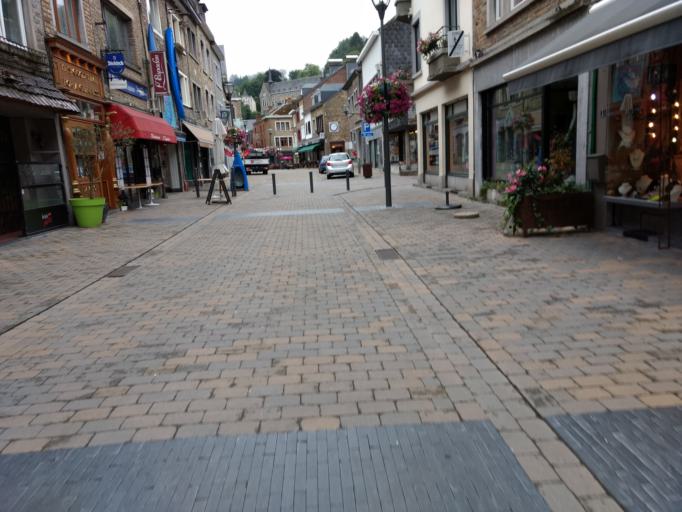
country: BE
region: Wallonia
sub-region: Province du Luxembourg
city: La Roche-en-Ardenne
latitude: 50.1822
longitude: 5.5755
